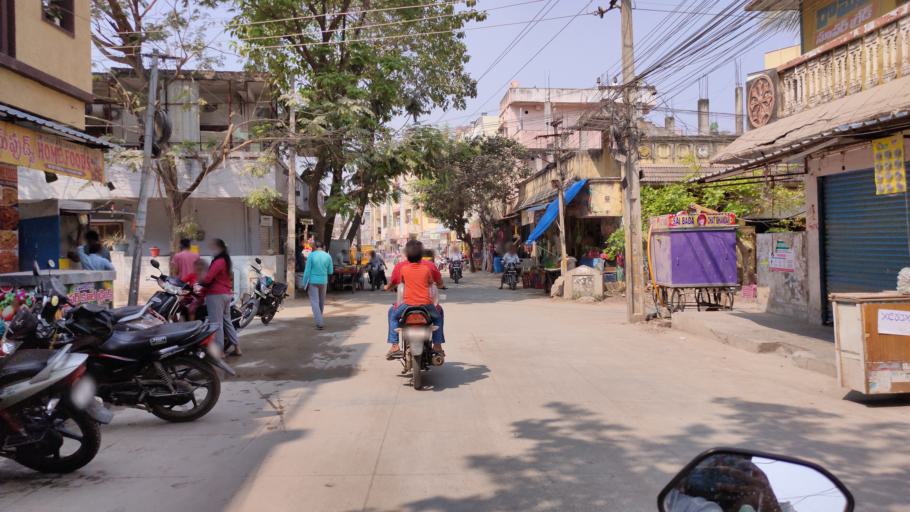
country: IN
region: Telangana
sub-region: Rangareddi
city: Quthbullapur
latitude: 17.4947
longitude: 78.4588
